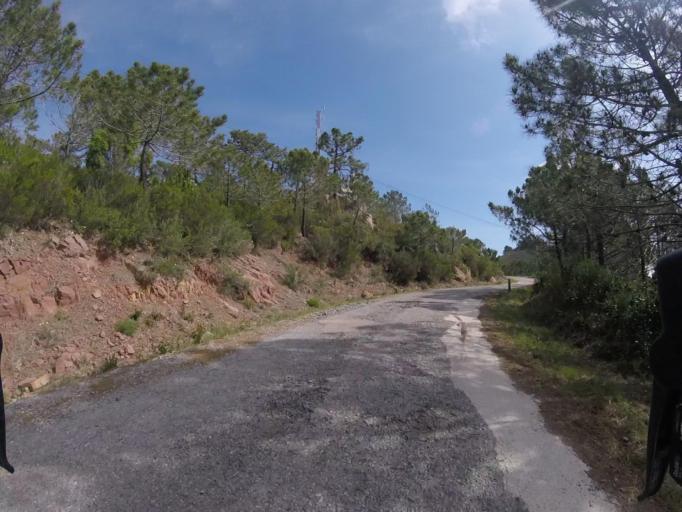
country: ES
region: Valencia
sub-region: Provincia de Castello
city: Benicassim
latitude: 40.0841
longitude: 0.0270
